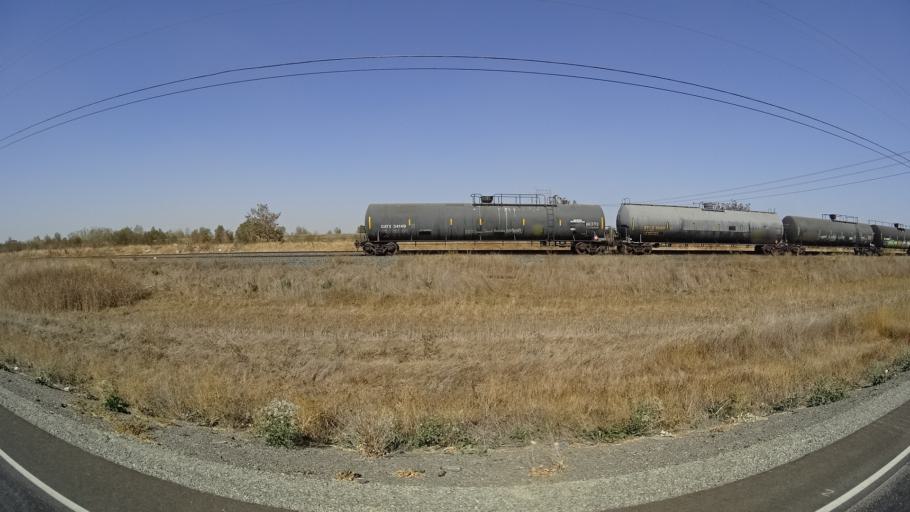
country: US
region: California
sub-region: Yolo County
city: Woodland
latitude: 38.6768
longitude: -121.6761
